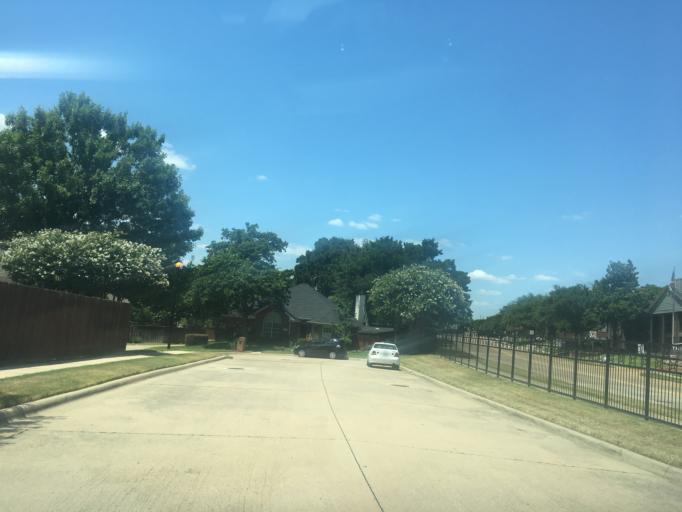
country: US
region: Texas
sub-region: Denton County
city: Lewisville
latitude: 33.0227
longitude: -96.9996
